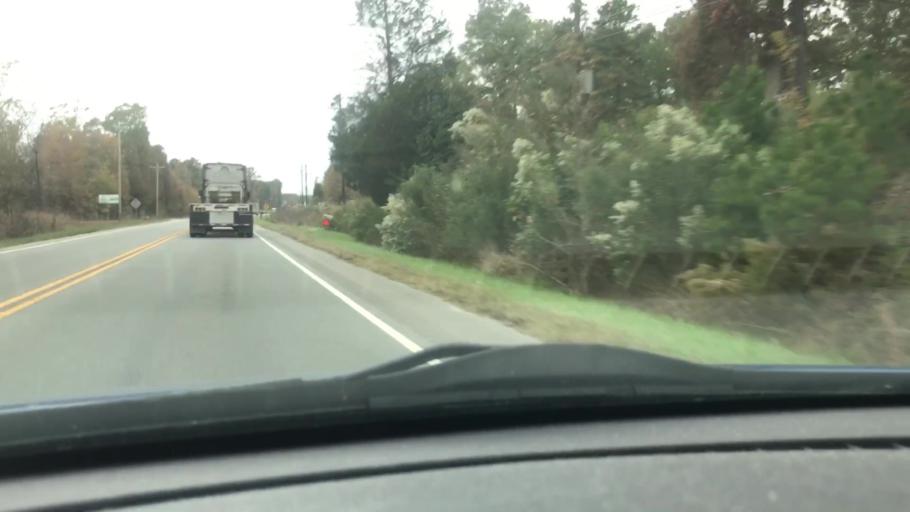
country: US
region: North Carolina
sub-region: Davidson County
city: Thomasville
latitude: 35.7778
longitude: -80.1179
